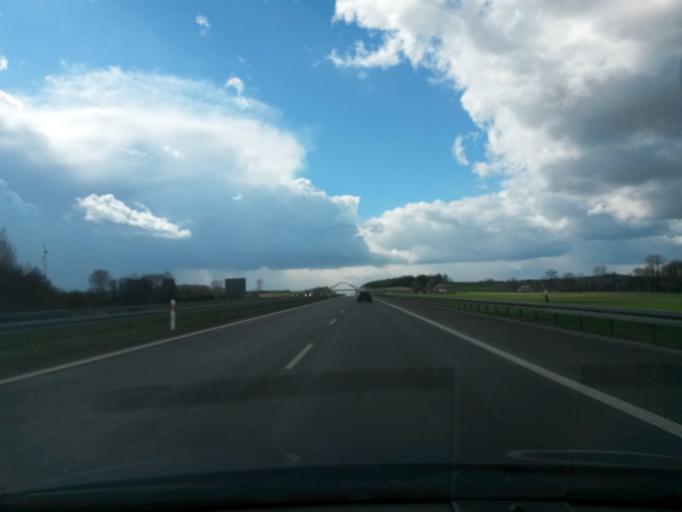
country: PL
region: Greater Poland Voivodeship
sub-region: Powiat kolski
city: Koscielec
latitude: 52.1423
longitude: 18.5814
